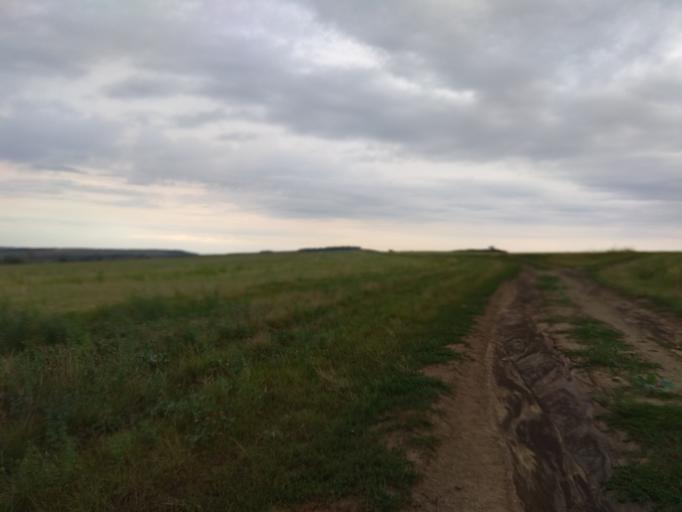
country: HU
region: Borsod-Abauj-Zemplen
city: Megyaszo
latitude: 48.1815
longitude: 21.0994
